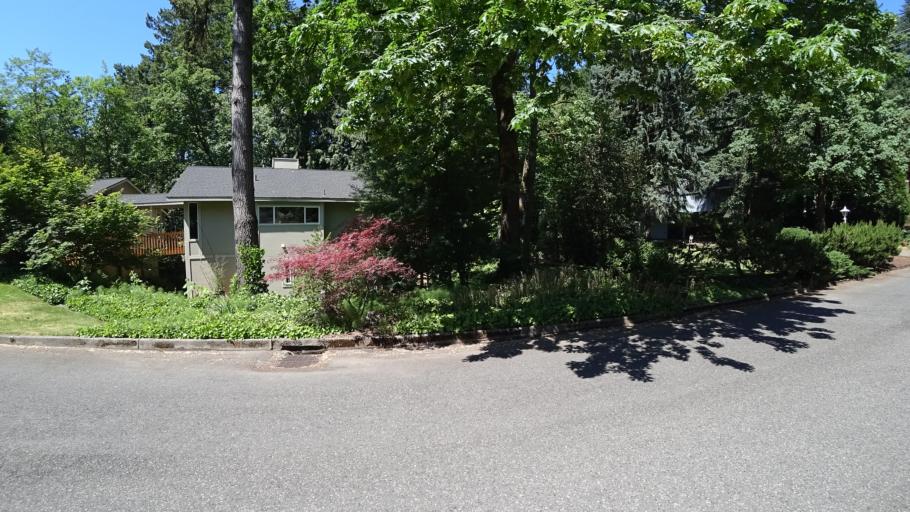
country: US
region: Oregon
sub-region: Washington County
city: Raleigh Hills
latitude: 45.4870
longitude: -122.7166
